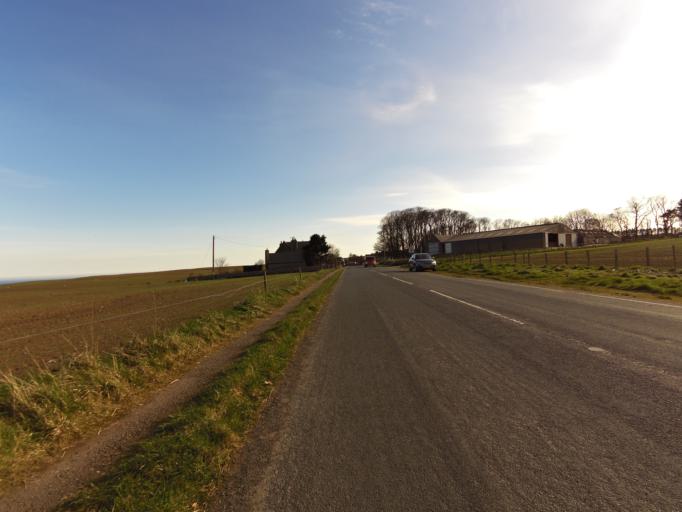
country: GB
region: Scotland
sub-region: Aberdeenshire
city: Stonehaven
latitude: 56.9465
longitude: -2.2056
